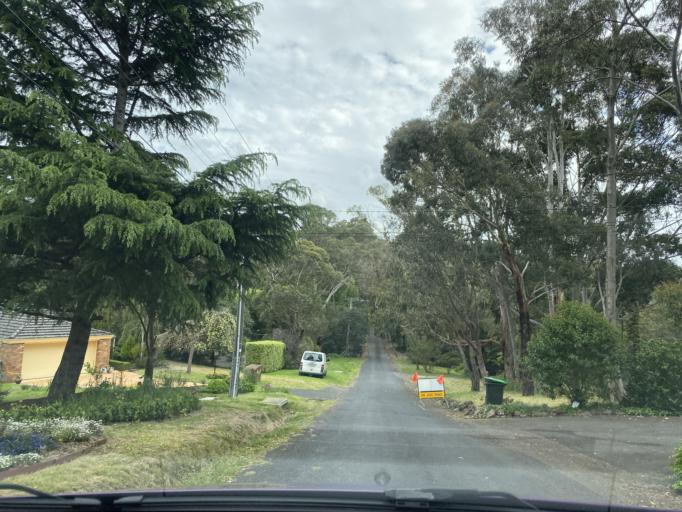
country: AU
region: Victoria
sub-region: Manningham
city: Templestowe Lower
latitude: -37.7653
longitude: 145.1292
